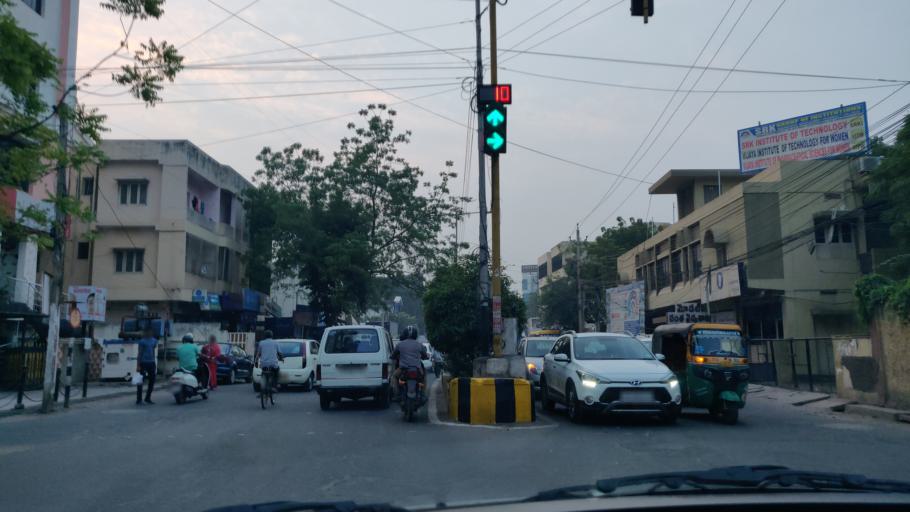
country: IN
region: Andhra Pradesh
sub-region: Krishna
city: Vijayawada
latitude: 16.5069
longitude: 80.6446
